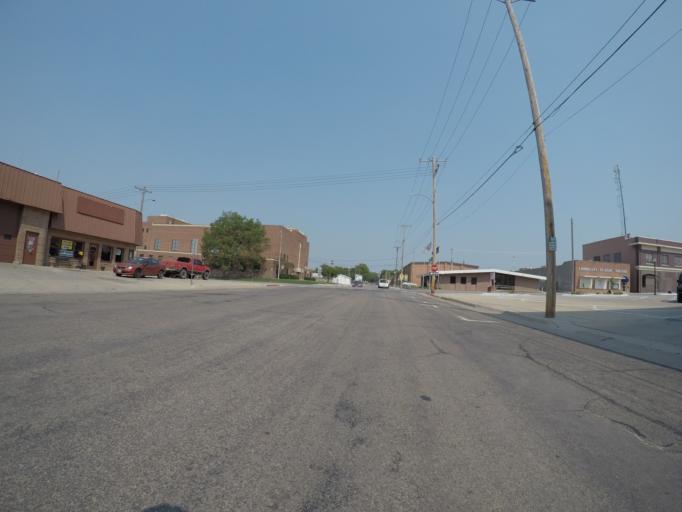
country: US
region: Nebraska
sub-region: Gage County
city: Beatrice
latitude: 40.2665
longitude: -96.7495
